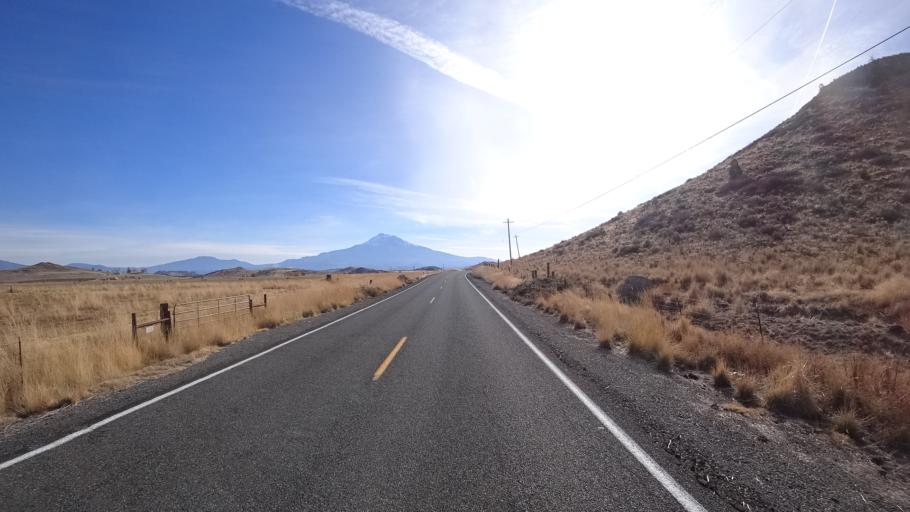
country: US
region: California
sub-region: Siskiyou County
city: Weed
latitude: 41.5368
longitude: -122.5217
